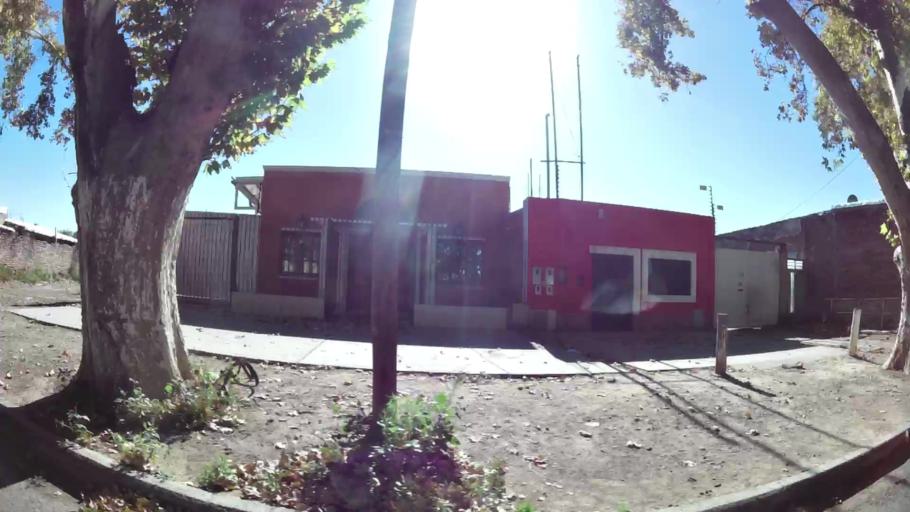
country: AR
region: Mendoza
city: Las Heras
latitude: -32.8383
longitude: -68.8252
